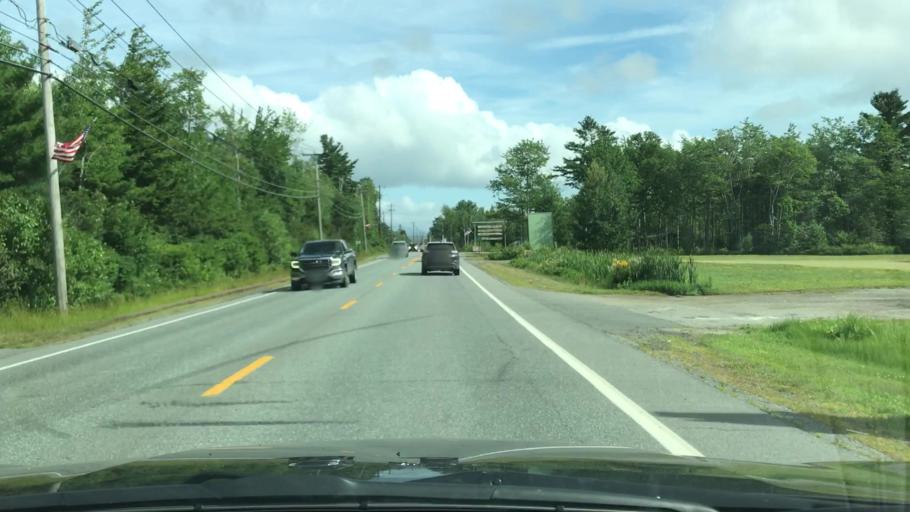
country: US
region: Maine
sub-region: Hancock County
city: Ellsworth
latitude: 44.5039
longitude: -68.3856
